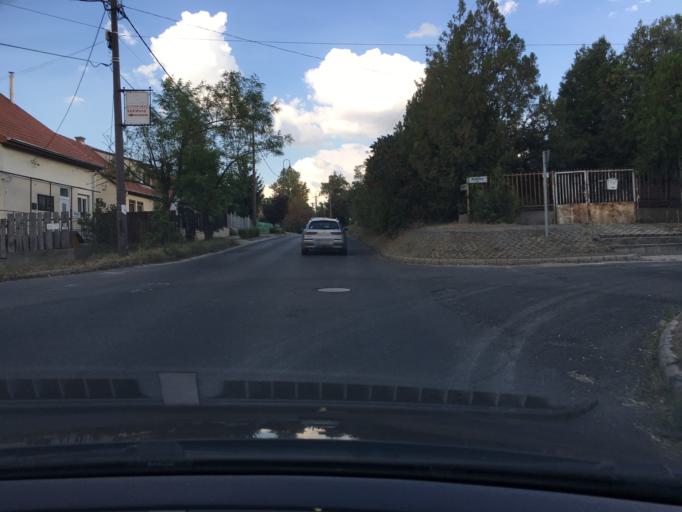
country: HU
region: Pest
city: Veresegyhaz
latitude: 47.6477
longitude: 19.3009
